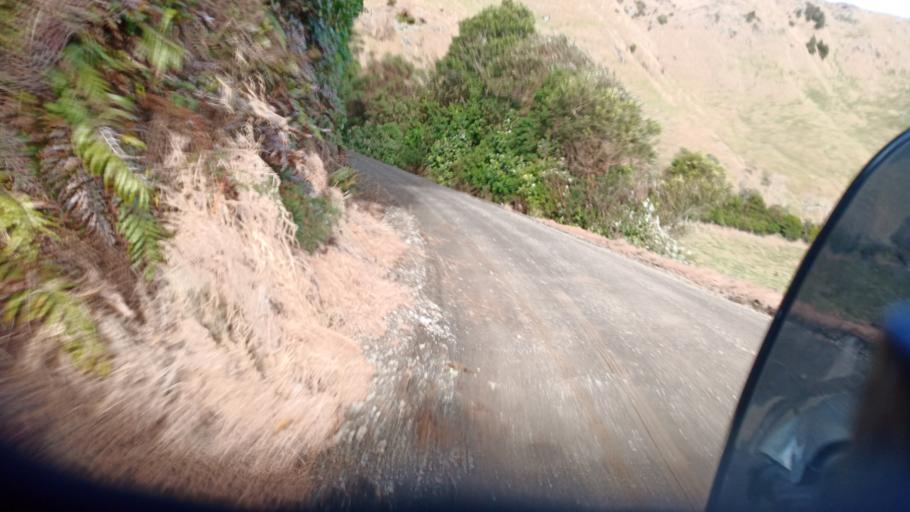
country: NZ
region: Gisborne
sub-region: Gisborne District
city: Gisborne
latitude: -38.4601
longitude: 177.5382
